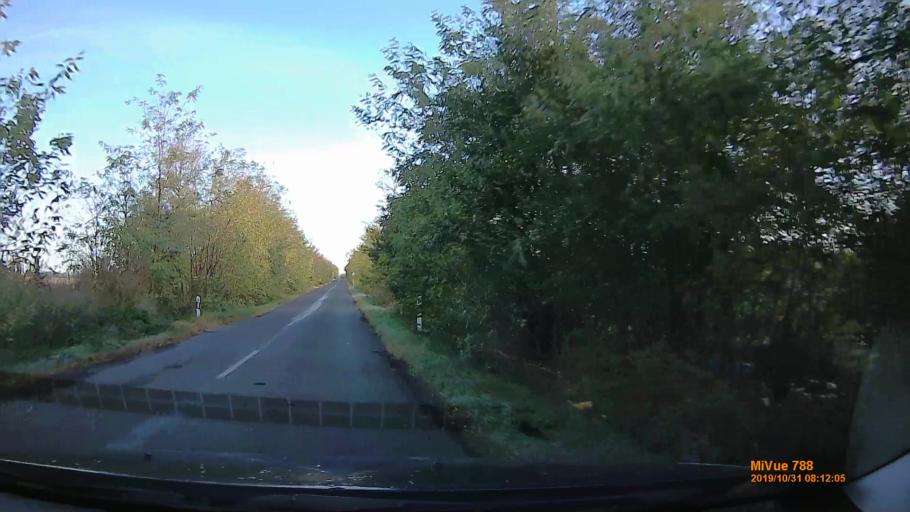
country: HU
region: Pest
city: Pilis
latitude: 47.3211
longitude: 19.5656
